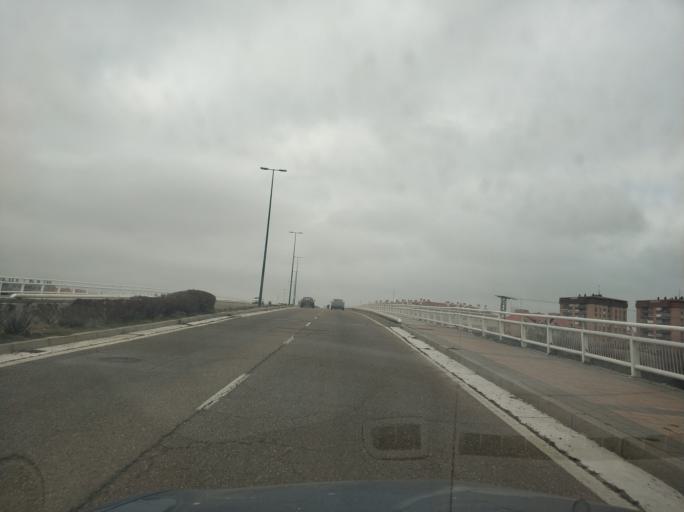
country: ES
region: Castille and Leon
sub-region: Provincia de Valladolid
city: Valladolid
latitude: 41.6206
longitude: -4.7387
